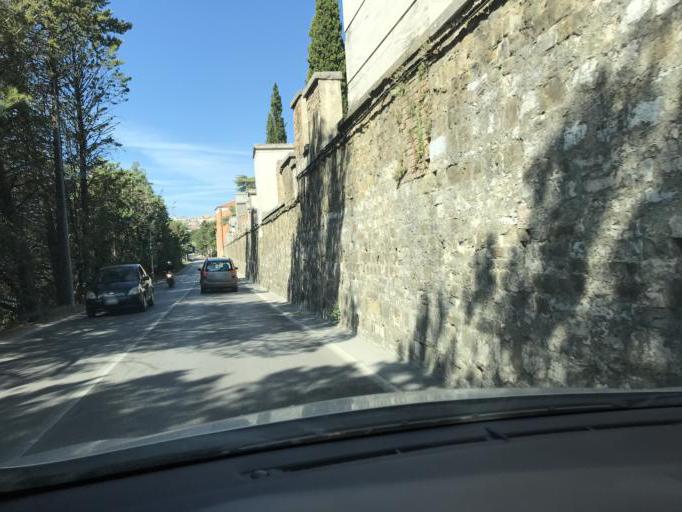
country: IT
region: Umbria
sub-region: Provincia di Perugia
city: Perugia
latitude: 43.1105
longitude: 12.4135
